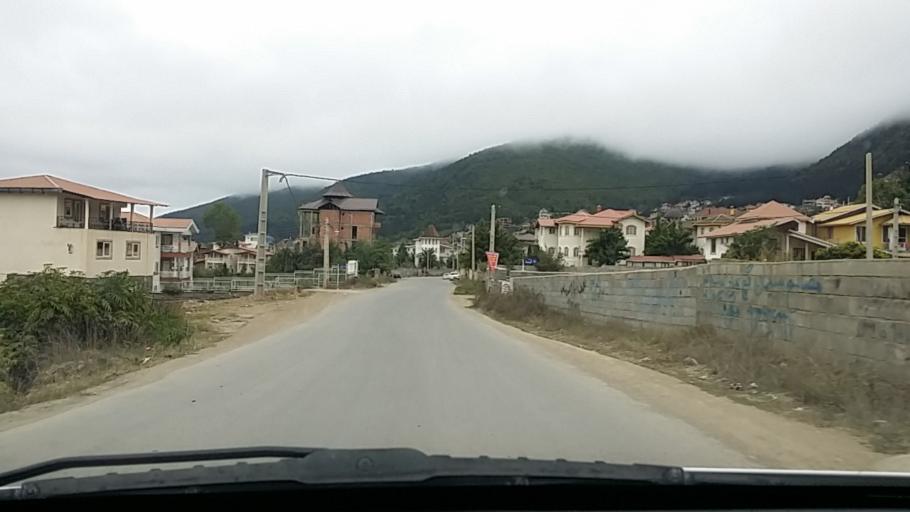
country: IR
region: Mazandaran
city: `Abbasabad
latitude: 36.4987
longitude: 51.1535
